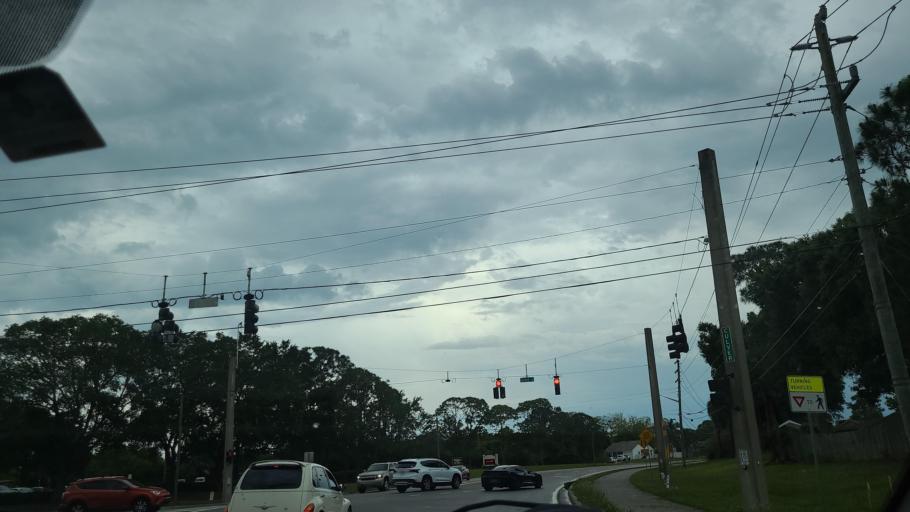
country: US
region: Florida
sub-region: Brevard County
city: West Melbourne
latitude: 28.0304
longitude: -80.6611
